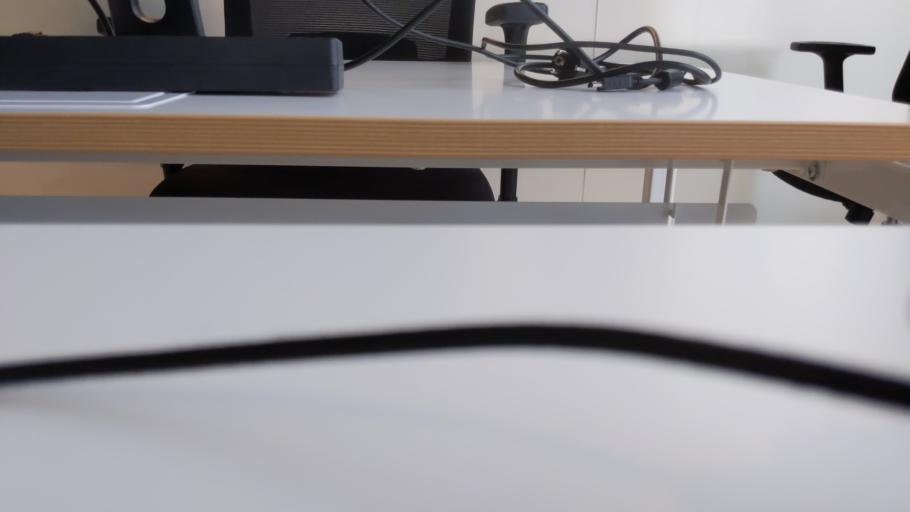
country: RU
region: Moskovskaya
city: Rogachevo
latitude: 56.4125
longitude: 37.0424
